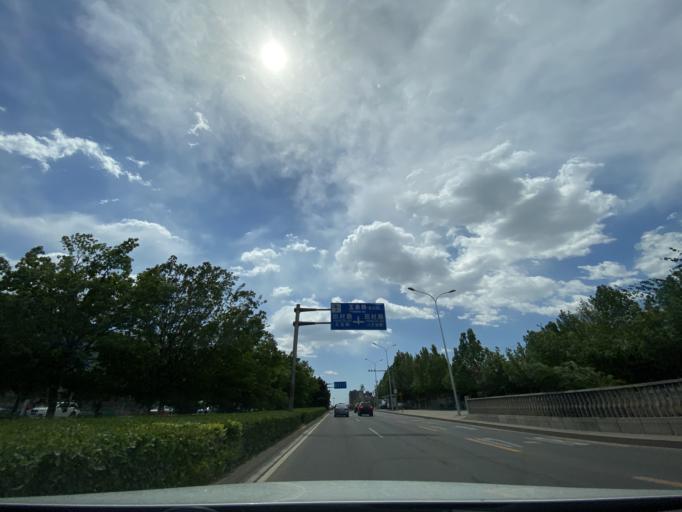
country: CN
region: Beijing
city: Sijiqing
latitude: 39.9305
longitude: 116.2468
